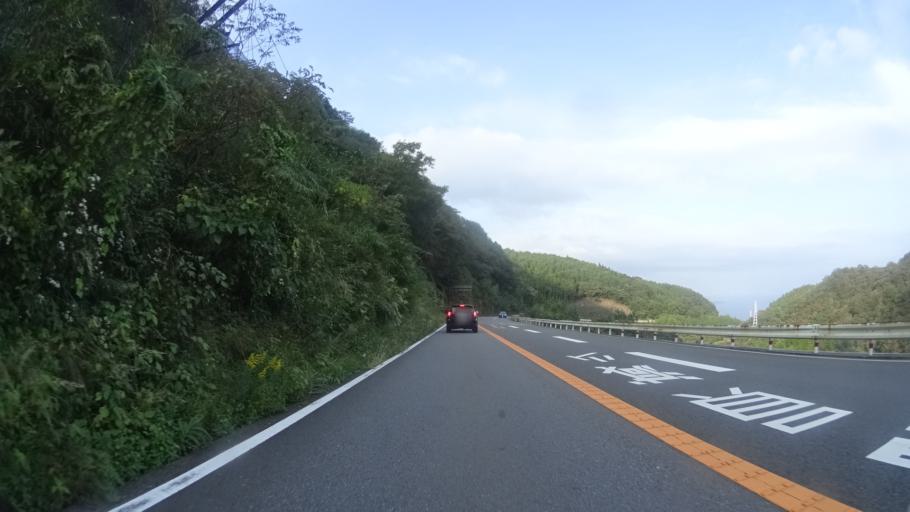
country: JP
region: Oita
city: Beppu
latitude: 33.2824
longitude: 131.4518
